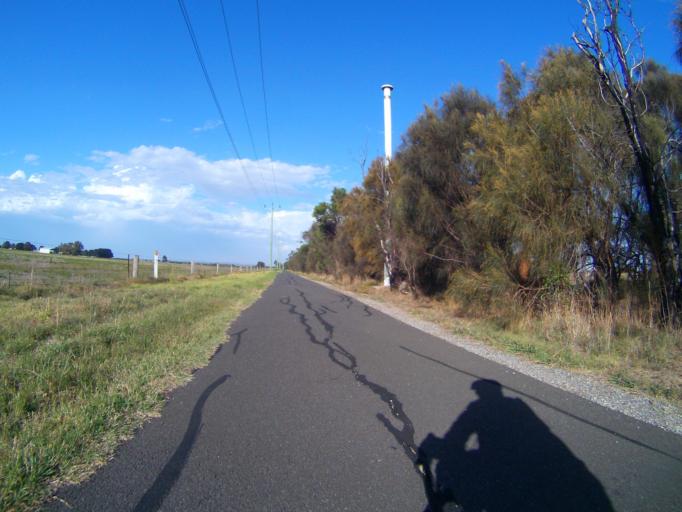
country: AU
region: Victoria
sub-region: Greater Geelong
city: Leopold
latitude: -38.1831
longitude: 144.4839
